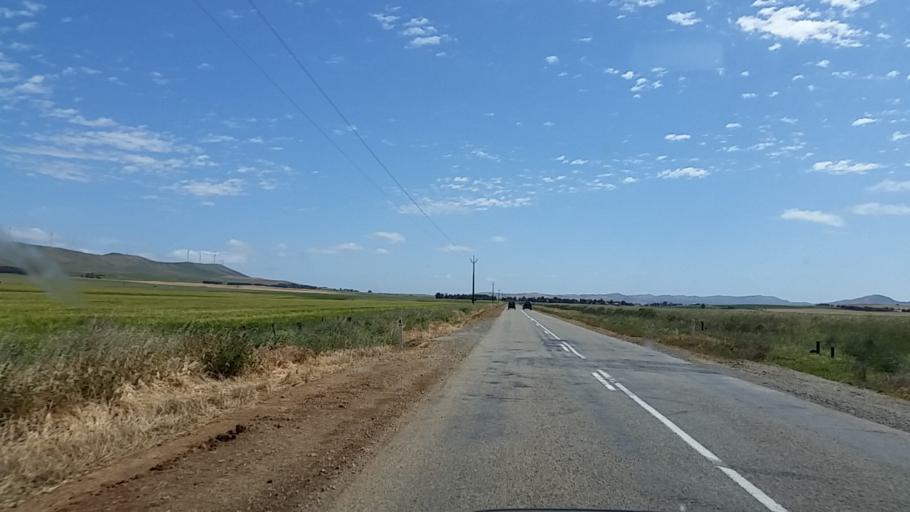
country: AU
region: South Australia
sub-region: Clare and Gilbert Valleys
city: Clare
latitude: -33.5716
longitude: 138.8891
